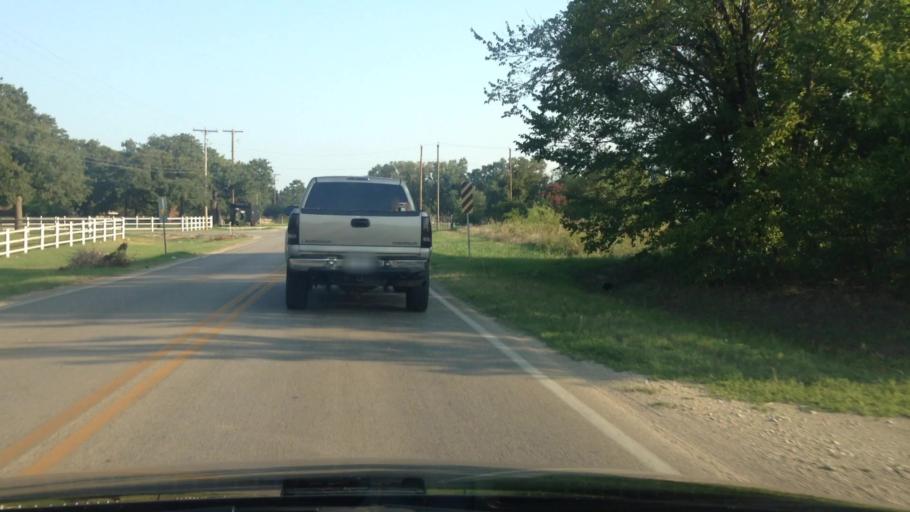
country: US
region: Texas
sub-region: Tarrant County
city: Everman
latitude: 32.6120
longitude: -97.2685
